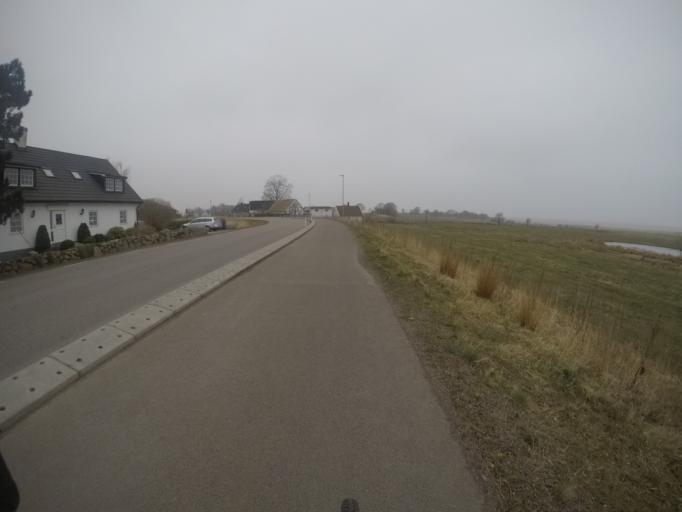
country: SE
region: Skane
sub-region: Angelholms Kommun
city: Vejbystrand
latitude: 56.2227
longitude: 12.7465
